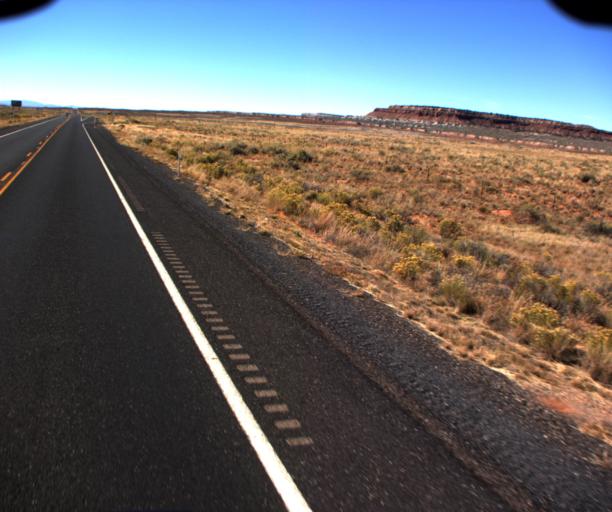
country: US
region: Arizona
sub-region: Coconino County
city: Fredonia
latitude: 36.9339
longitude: -112.5565
